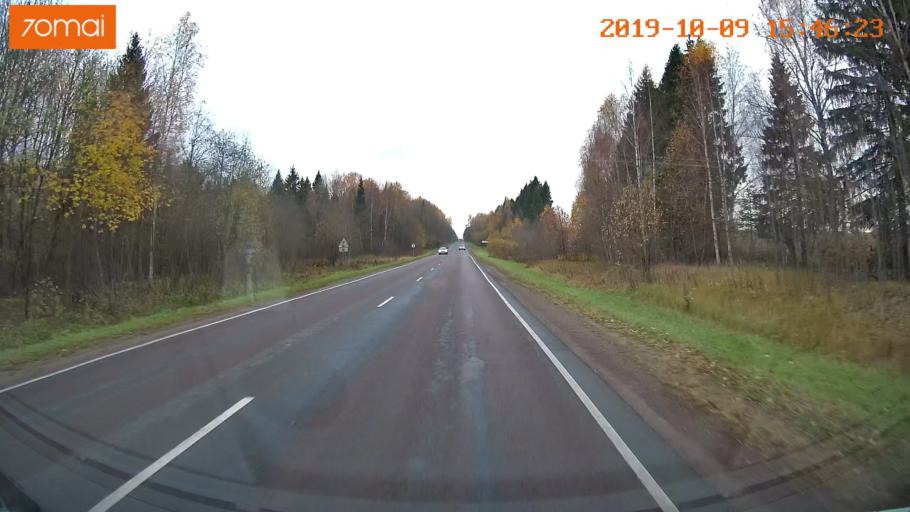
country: RU
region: Kostroma
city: Oktyabr'skiy
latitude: 57.8252
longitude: 41.0449
